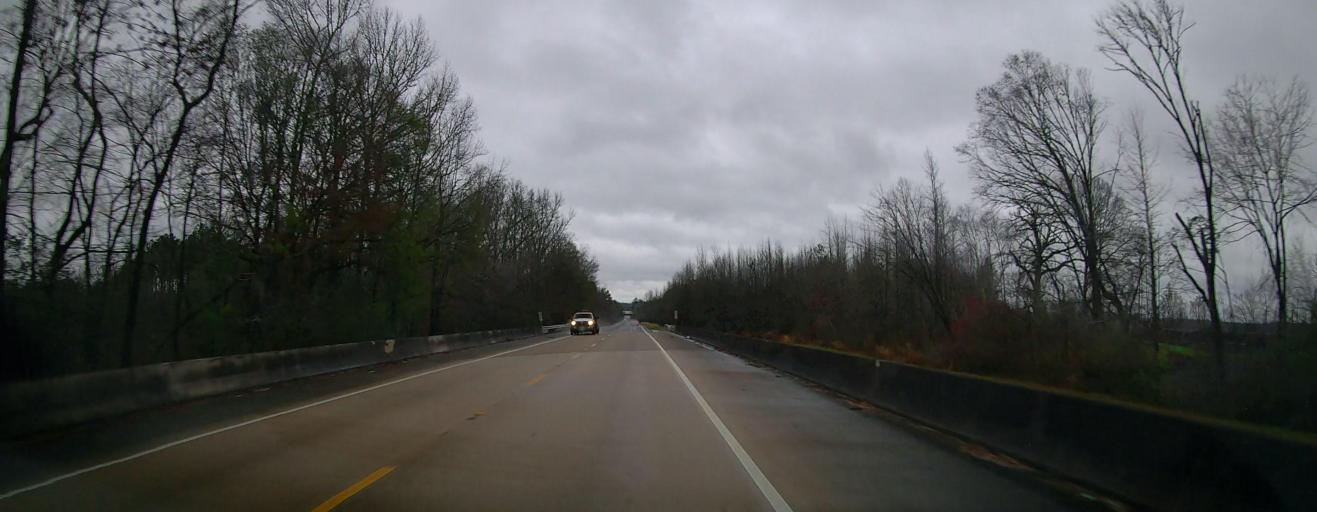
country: US
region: Alabama
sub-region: Chilton County
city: Thorsby
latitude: 32.7563
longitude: -86.8717
